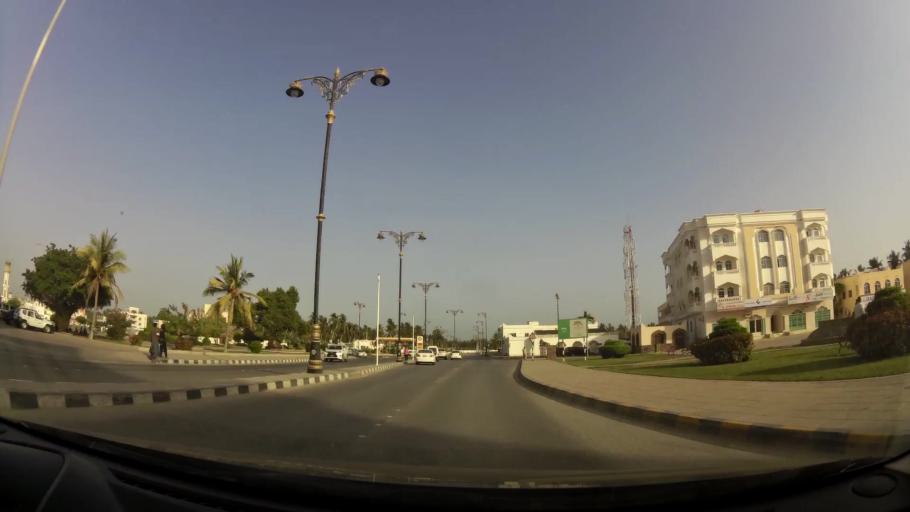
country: OM
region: Zufar
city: Salalah
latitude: 17.0103
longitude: 54.0947
